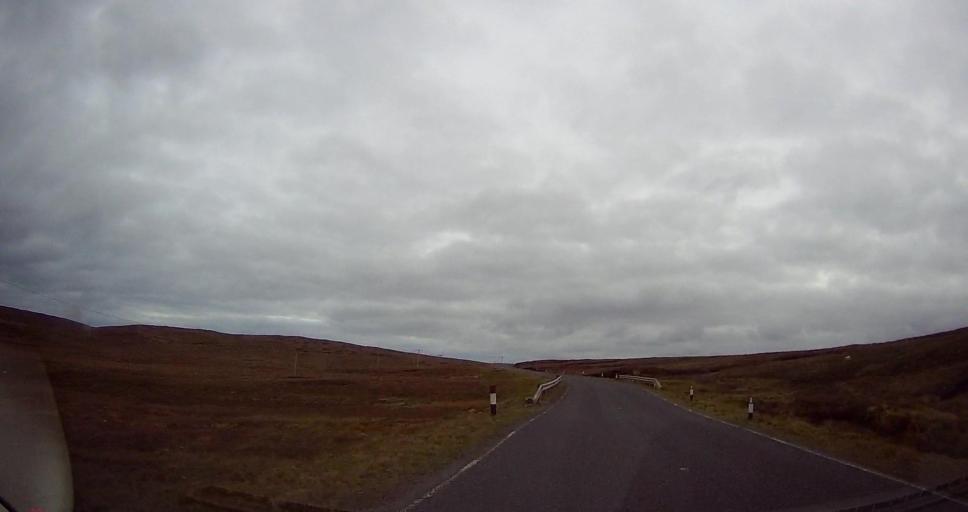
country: GB
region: Scotland
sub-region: Shetland Islands
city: Shetland
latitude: 60.6358
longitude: -1.0663
